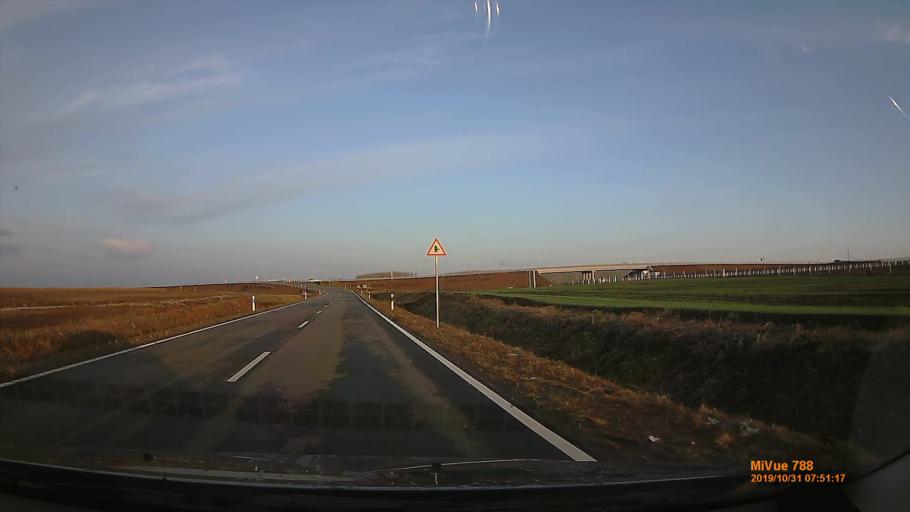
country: HU
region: Pest
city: Pilis
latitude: 47.3077
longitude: 19.5580
